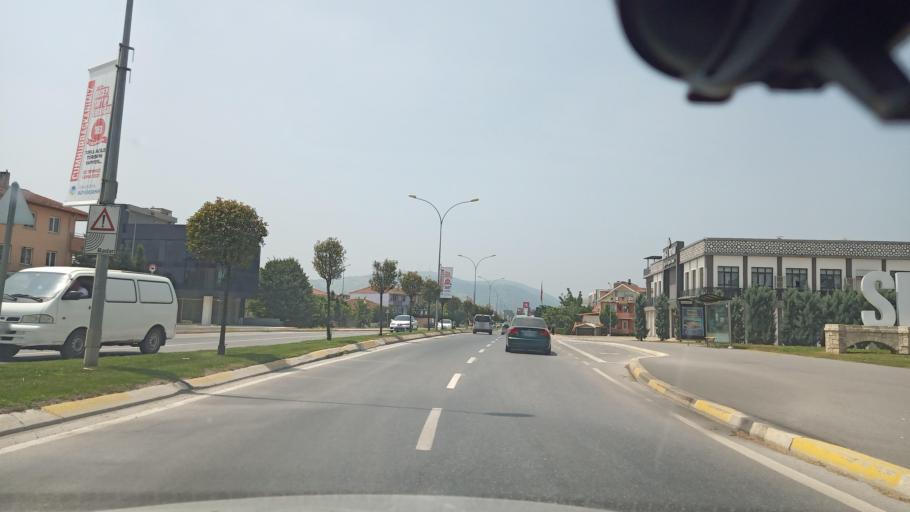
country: TR
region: Sakarya
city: Adapazari
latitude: 40.7875
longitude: 30.3724
